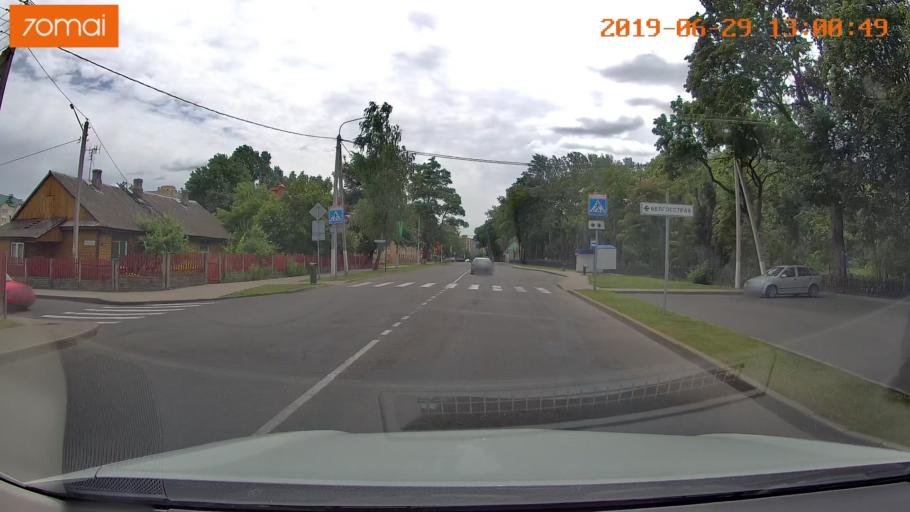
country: BY
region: Minsk
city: Slutsk
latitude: 53.0424
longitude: 27.5582
